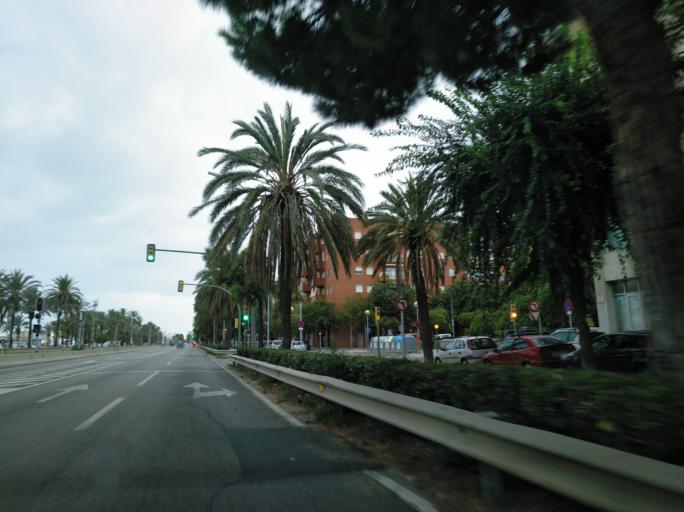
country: ES
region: Catalonia
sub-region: Provincia de Barcelona
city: Mataro
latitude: 41.5393
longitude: 2.4537
